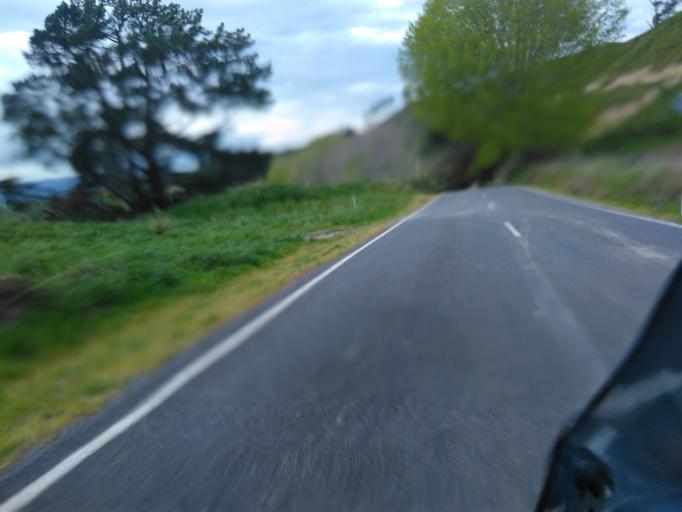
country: NZ
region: Hawke's Bay
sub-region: Wairoa District
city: Wairoa
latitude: -38.9234
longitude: 177.4308
